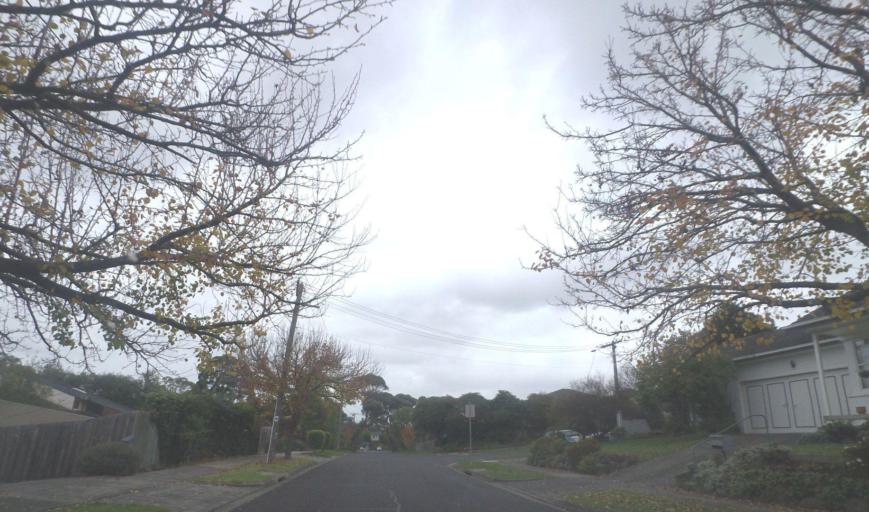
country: AU
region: Victoria
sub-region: Manningham
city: Doncaster
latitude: -37.7804
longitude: 145.1141
